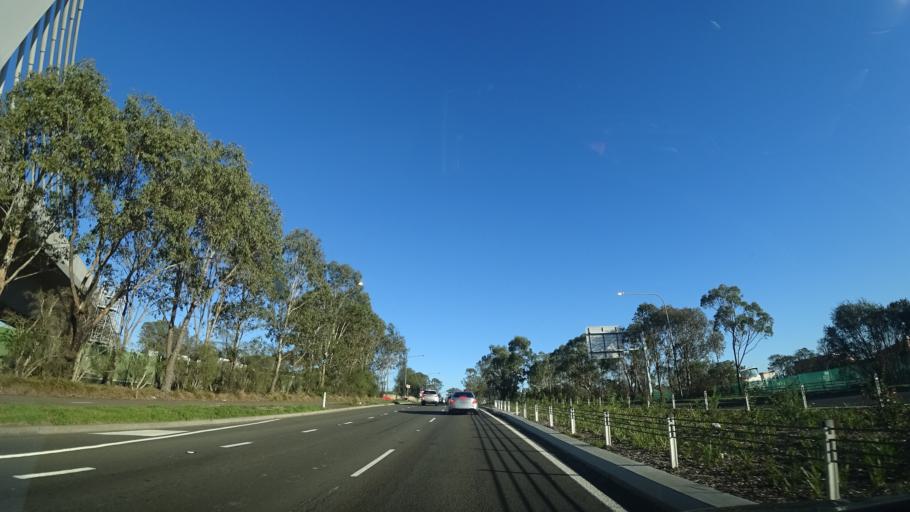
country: AU
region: New South Wales
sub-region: Blacktown
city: Rouse Hill
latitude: -33.6889
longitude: 150.9210
